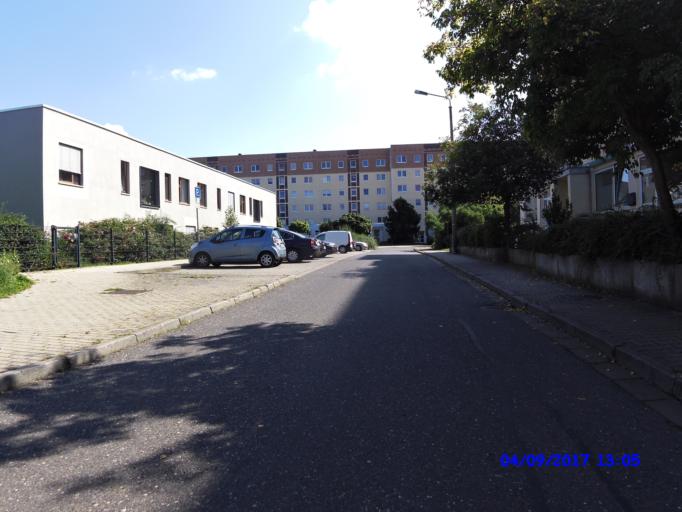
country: DE
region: Saxony
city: Taucha
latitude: 51.3522
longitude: 12.4600
